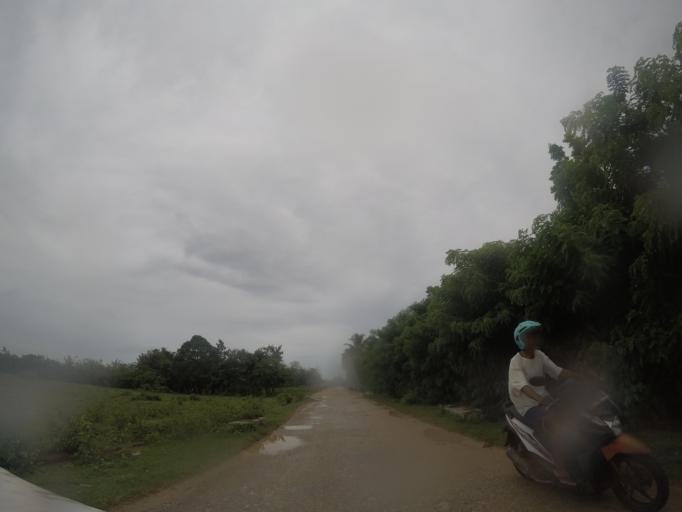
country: TL
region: Lautem
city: Lospalos
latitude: -8.5103
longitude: 127.0015
